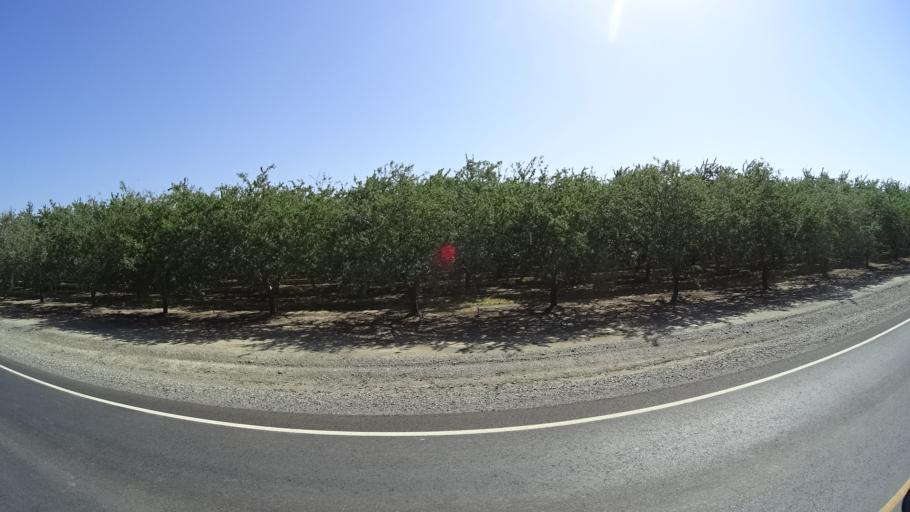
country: US
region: California
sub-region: Glenn County
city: Hamilton City
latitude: 39.6567
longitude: -122.0650
